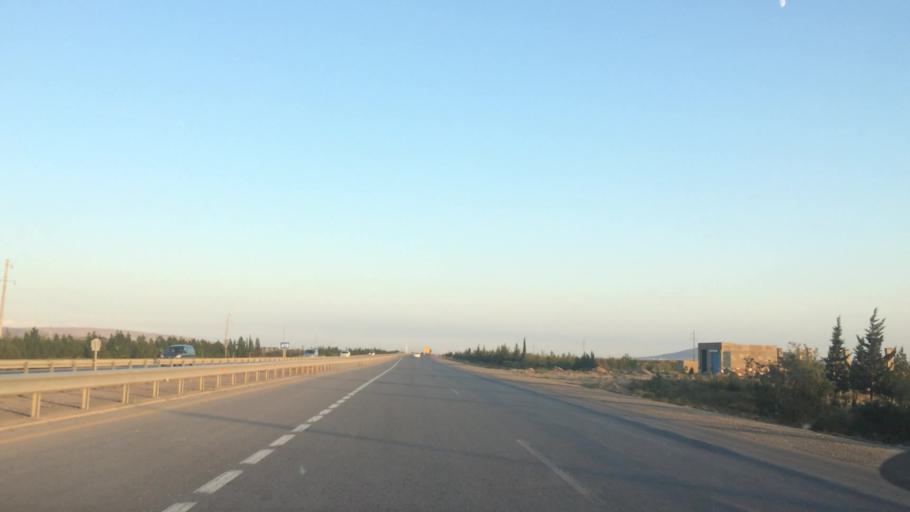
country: AZ
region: Haciqabul
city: Haciqabul
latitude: 40.0056
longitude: 49.1610
